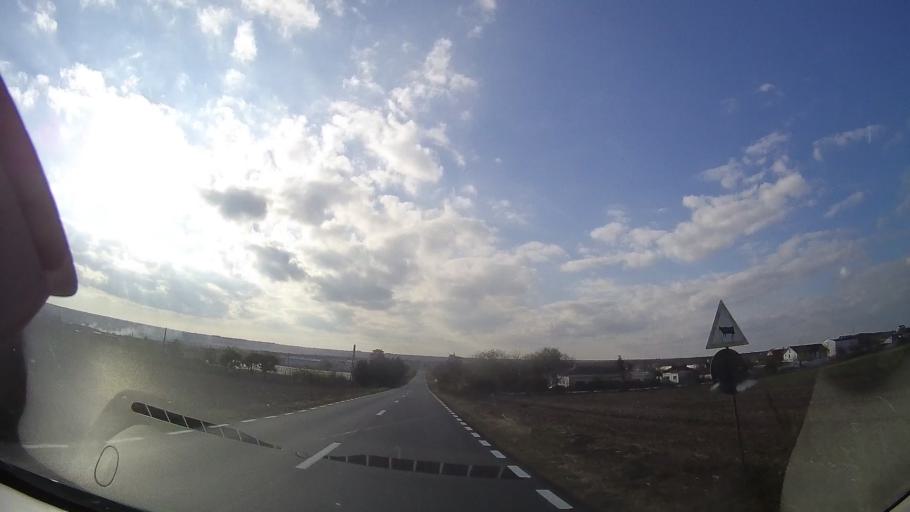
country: RO
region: Constanta
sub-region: Comuna Limanu
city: Limanu
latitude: 43.8246
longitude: 28.4930
